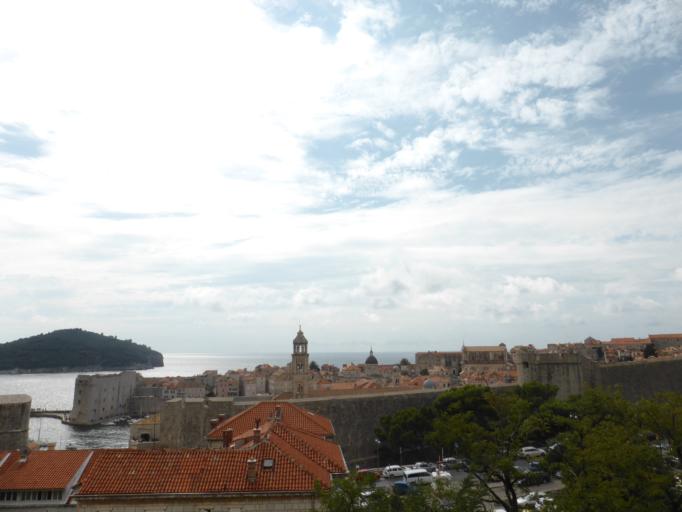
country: HR
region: Dubrovacko-Neretvanska
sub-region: Grad Dubrovnik
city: Dubrovnik
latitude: 42.6429
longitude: 18.1116
